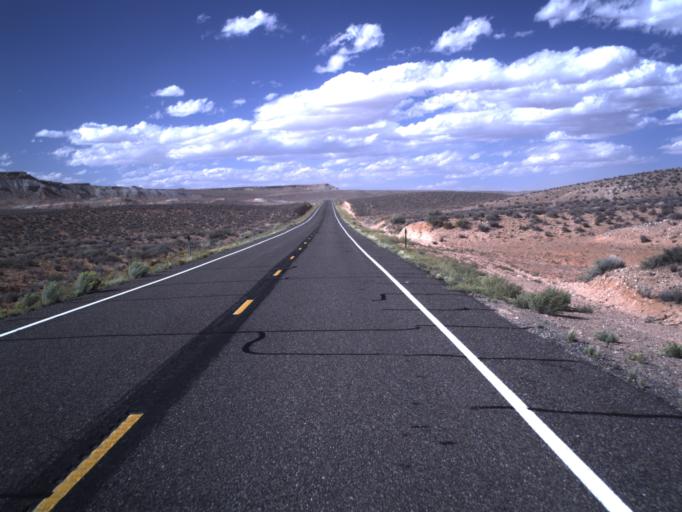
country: US
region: Utah
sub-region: Wayne County
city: Loa
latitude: 38.0895
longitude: -110.6173
